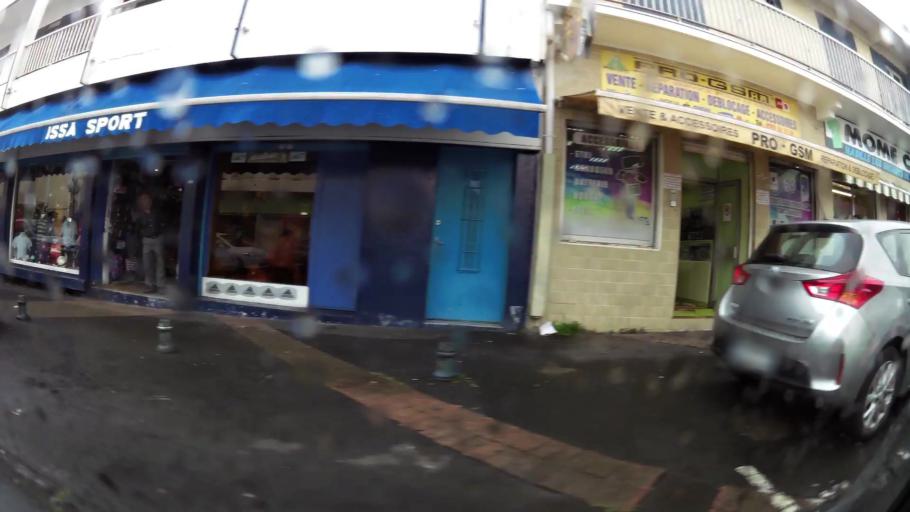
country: RE
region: Reunion
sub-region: Reunion
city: Saint-Andre
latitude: -20.9590
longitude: 55.6500
